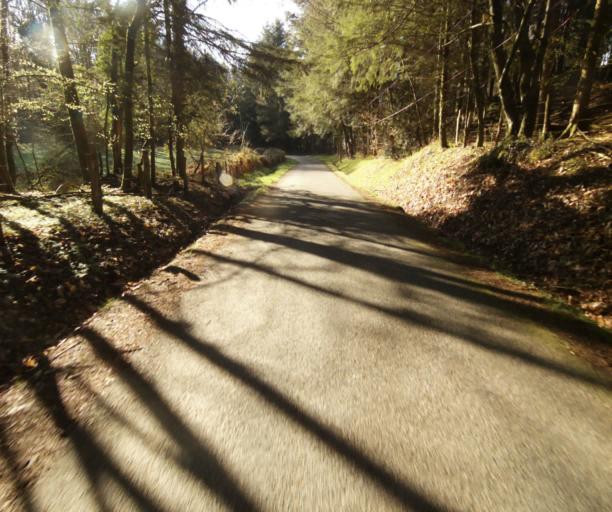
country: FR
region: Limousin
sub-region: Departement de la Correze
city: Laguenne
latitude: 45.2807
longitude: 1.8562
